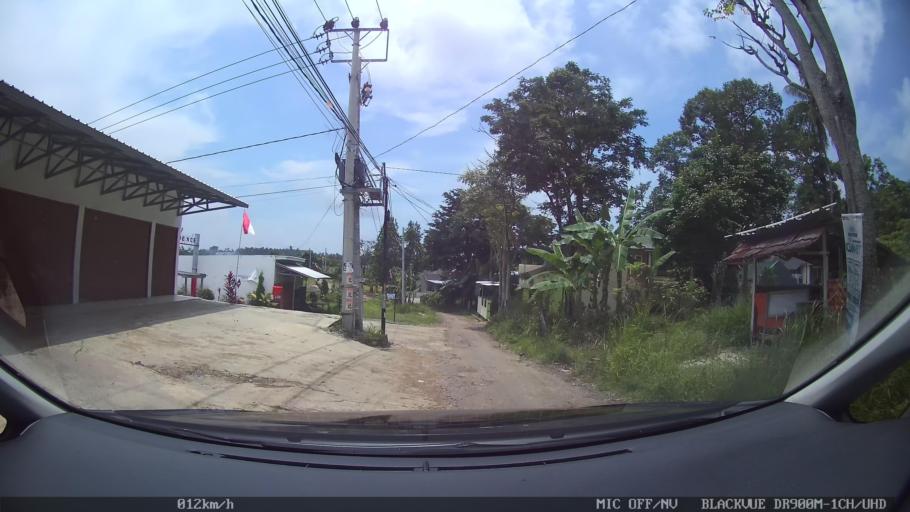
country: ID
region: Lampung
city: Bandarlampung
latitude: -5.4116
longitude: 105.2018
